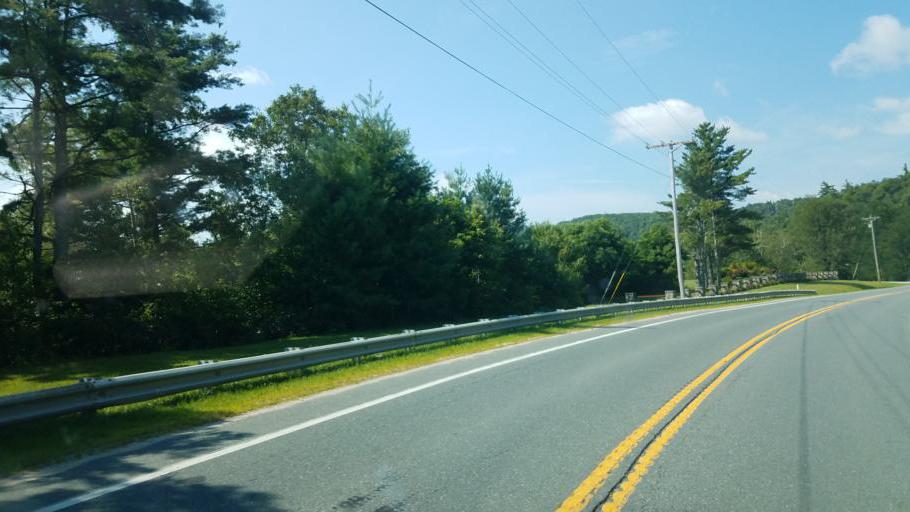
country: US
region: North Carolina
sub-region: Avery County
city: Newland
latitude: 35.9754
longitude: -81.8926
